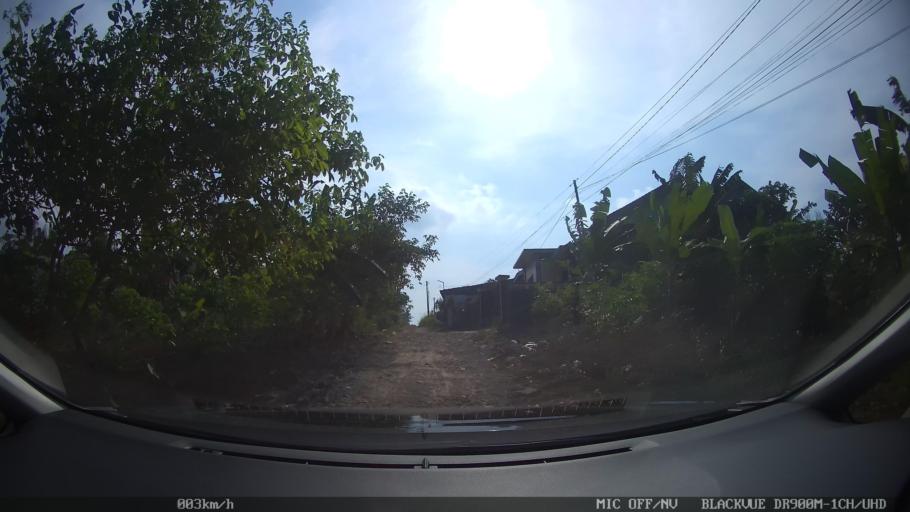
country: ID
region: Lampung
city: Kedaton
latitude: -5.3829
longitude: 105.2276
